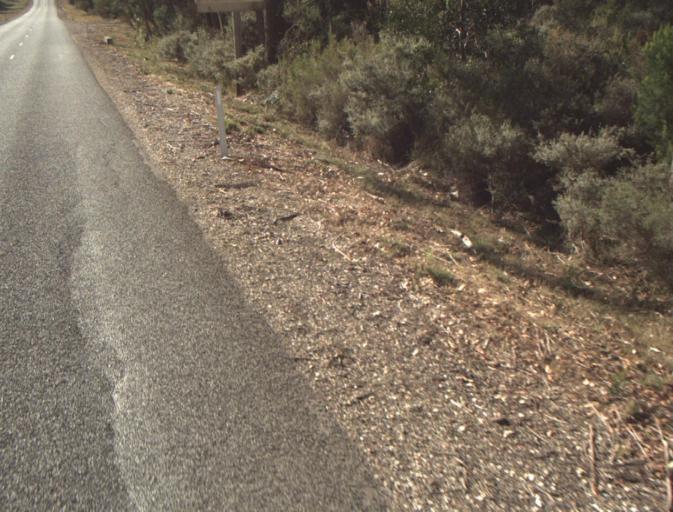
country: AU
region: Tasmania
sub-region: Launceston
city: Mayfield
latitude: -41.2981
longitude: 147.1329
